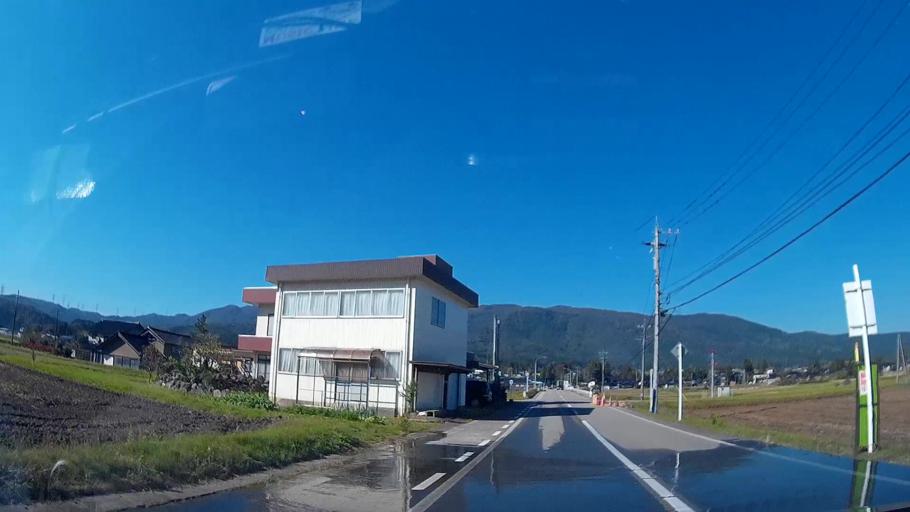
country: JP
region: Toyama
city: Fukumitsu
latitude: 36.5215
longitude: 136.8538
